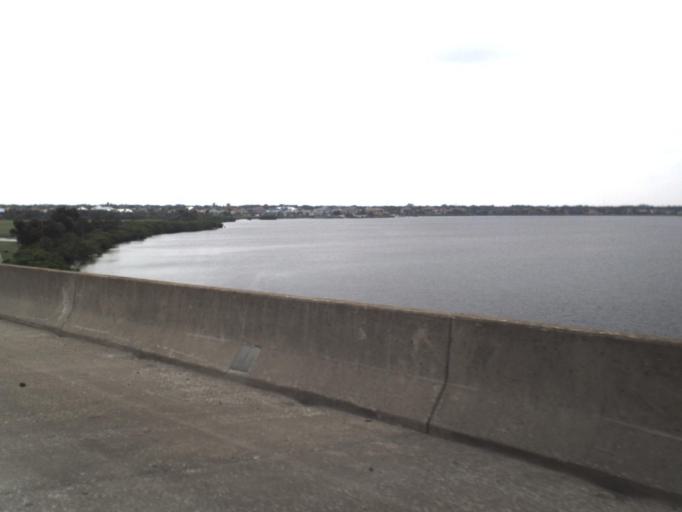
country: US
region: Florida
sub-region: Manatee County
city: Ellenton
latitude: 27.5212
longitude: -82.5050
